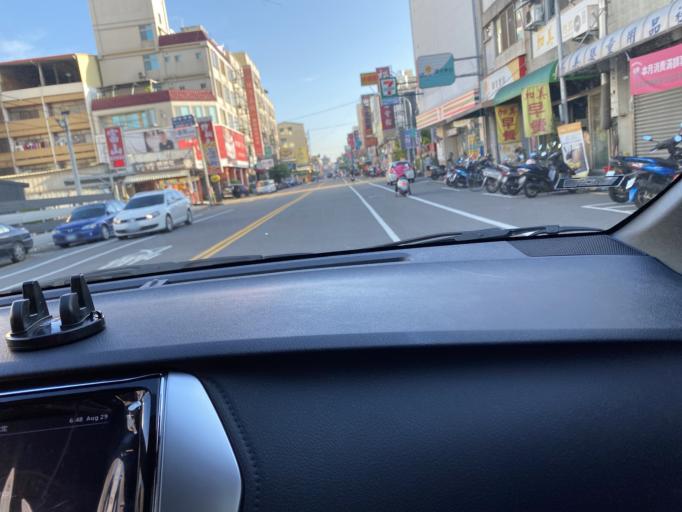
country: TW
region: Taiwan
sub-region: Changhua
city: Chang-hua
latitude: 24.0683
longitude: 120.5354
